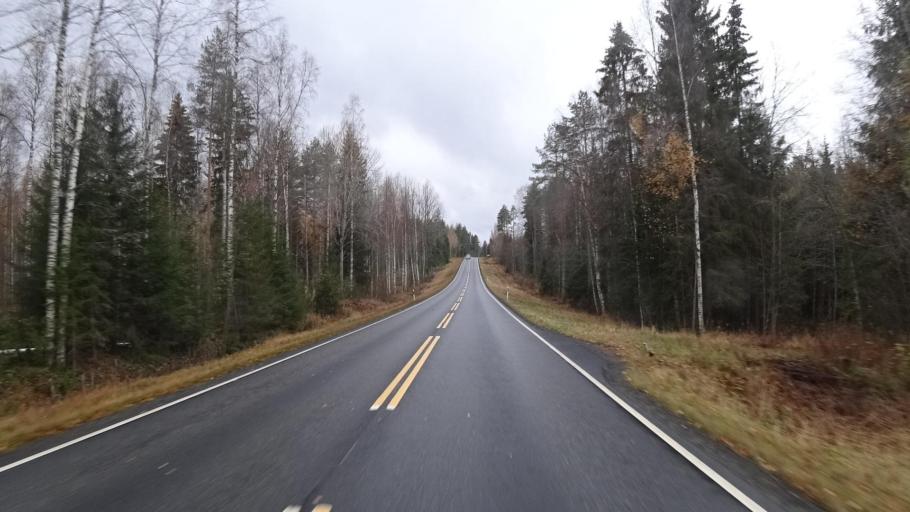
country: FI
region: Southern Savonia
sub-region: Mikkeli
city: Kangasniemi
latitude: 62.1690
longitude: 26.8509
